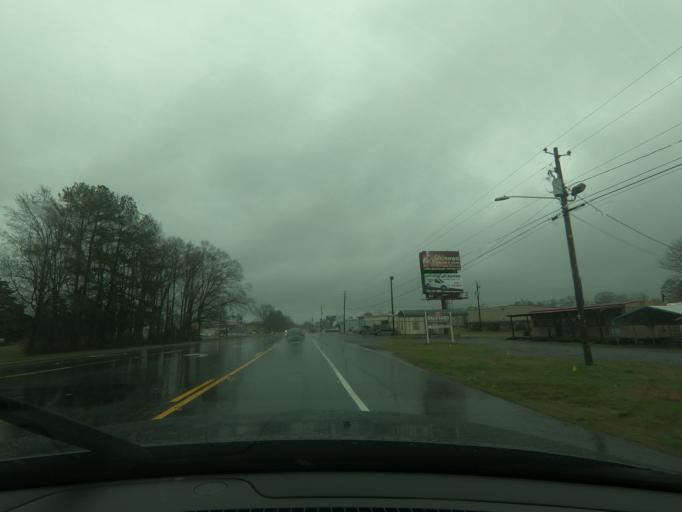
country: US
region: Georgia
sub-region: Bartow County
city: Adairsville
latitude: 34.3752
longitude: -84.9315
